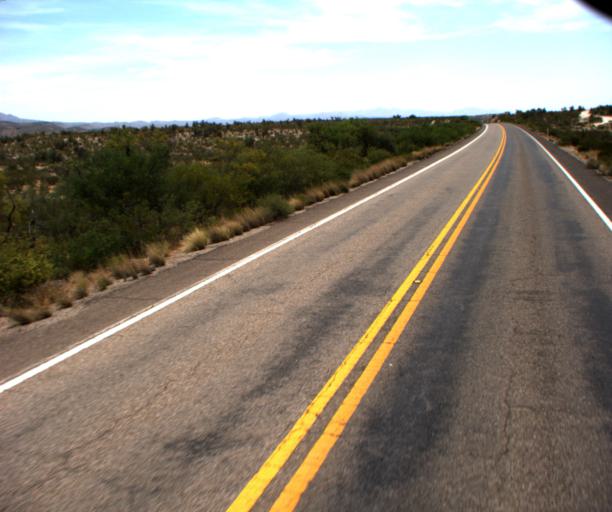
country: US
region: Arizona
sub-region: Gila County
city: Peridot
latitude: 33.2706
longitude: -110.3199
